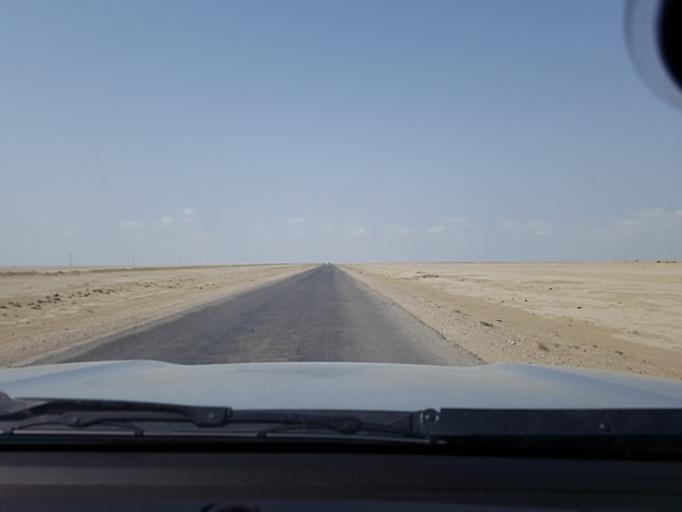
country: TM
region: Balkan
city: Gumdag
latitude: 38.6744
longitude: 54.4093
